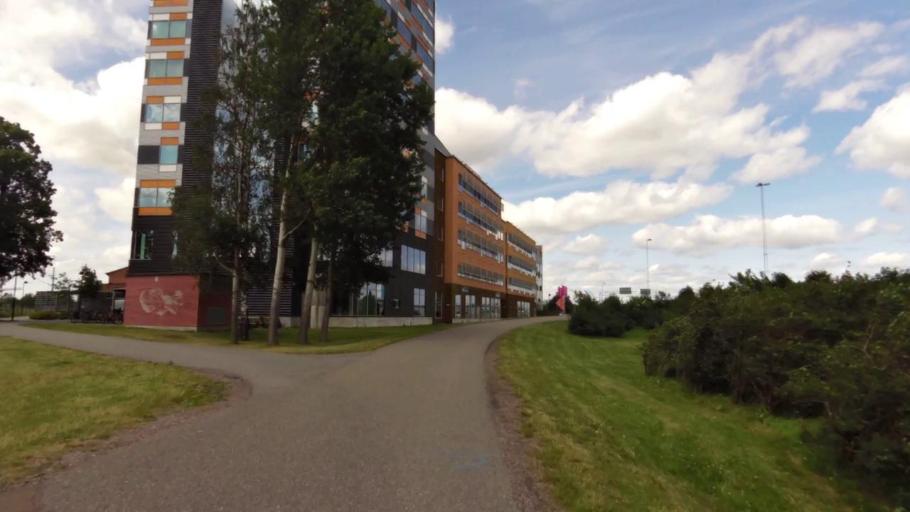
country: SE
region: OEstergoetland
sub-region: Linkopings Kommun
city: Linkoping
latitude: 58.4216
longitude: 15.6168
